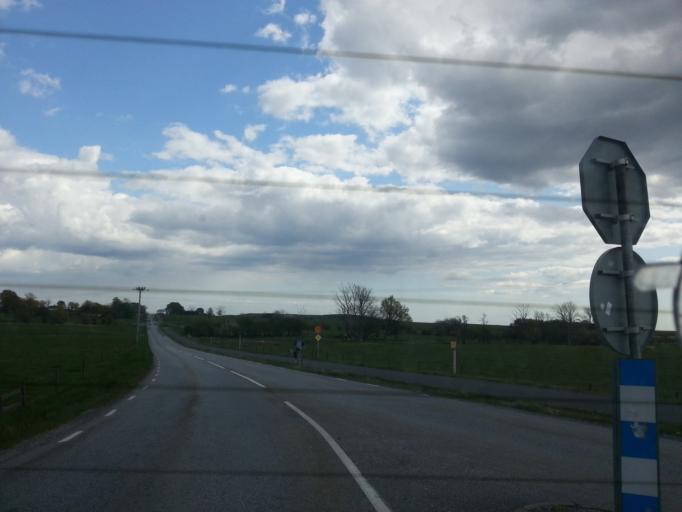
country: SE
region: Skane
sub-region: Ystads Kommun
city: Kopingebro
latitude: 55.4320
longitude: 13.9726
